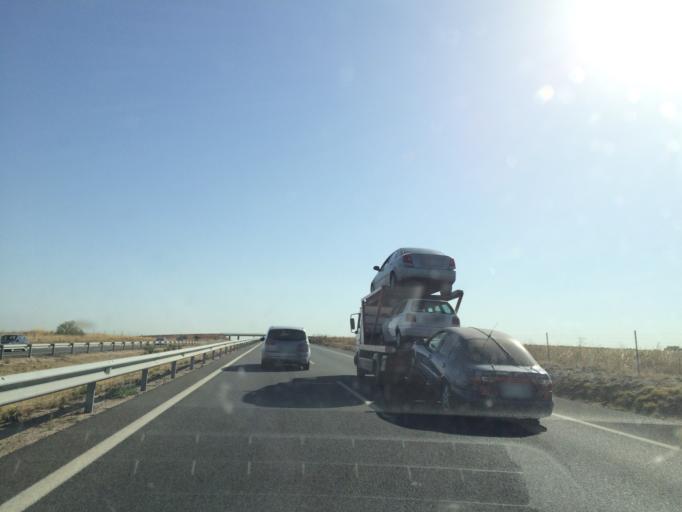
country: ES
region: Castille-La Mancha
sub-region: Province of Toledo
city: Las Ventas de Retamosa
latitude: 40.1689
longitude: -4.1637
